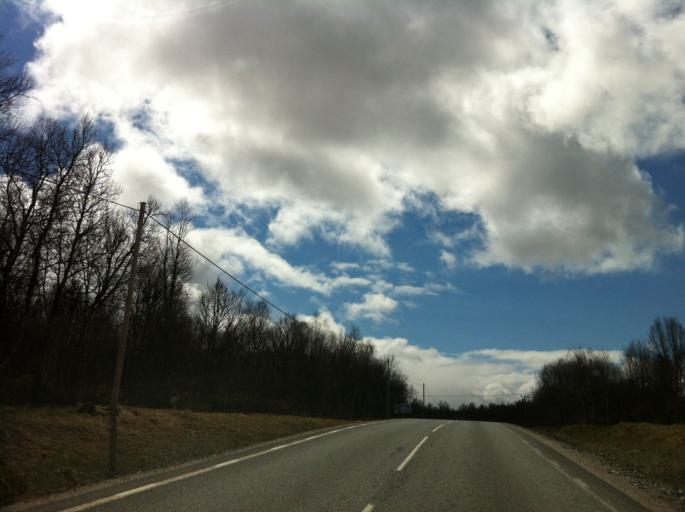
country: NO
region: Sor-Trondelag
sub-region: Tydal
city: Aas
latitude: 62.6641
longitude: 12.4292
